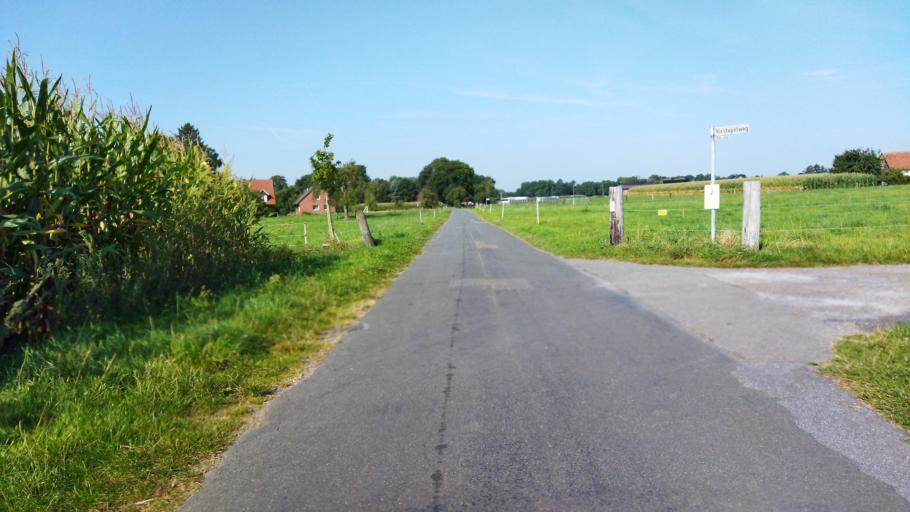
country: DE
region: North Rhine-Westphalia
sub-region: Regierungsbezirk Munster
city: Lienen
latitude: 52.1443
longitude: 7.9560
